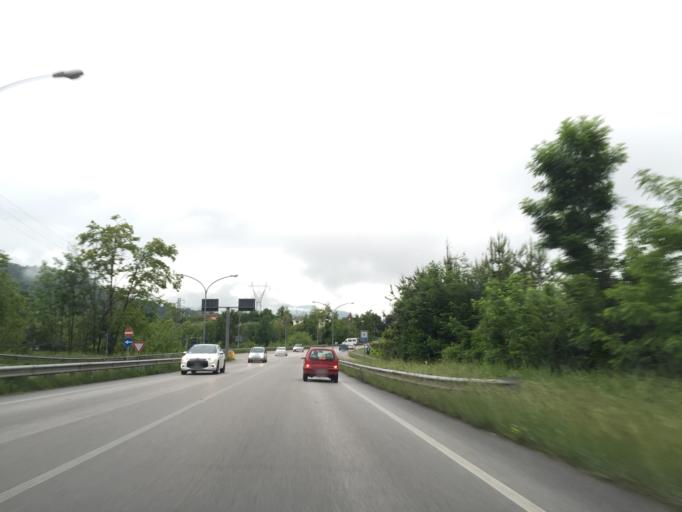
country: IT
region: Veneto
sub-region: Provincia di Belluno
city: Limana
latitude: 46.1091
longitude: 12.1990
